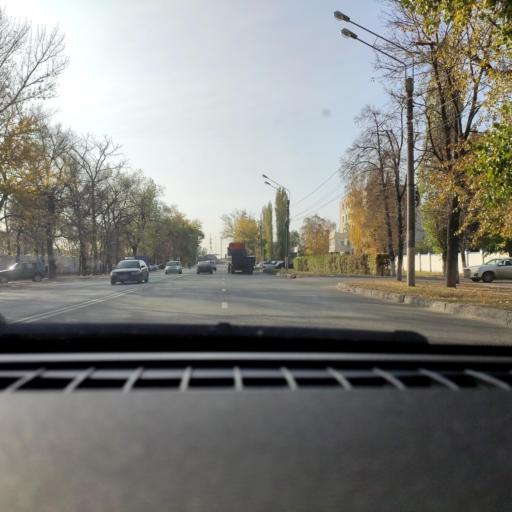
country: RU
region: Voronezj
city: Voronezh
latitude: 51.6501
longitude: 39.2693
